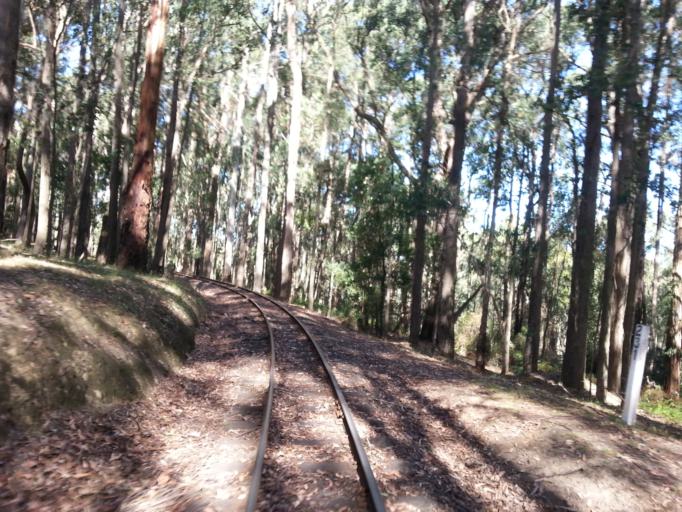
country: AU
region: Victoria
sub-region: Cardinia
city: Cockatoo
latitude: -37.9480
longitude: 145.5082
